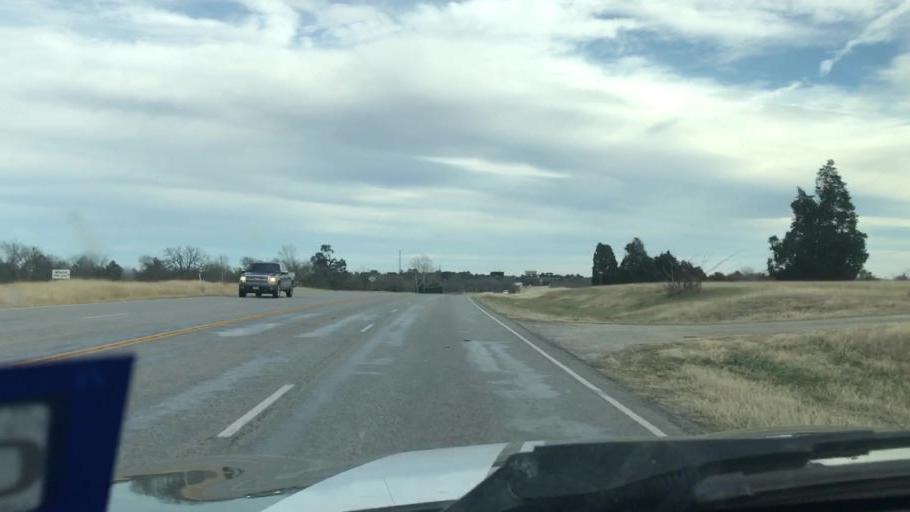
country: US
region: Texas
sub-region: Bastrop County
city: Camp Swift
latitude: 30.2965
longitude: -97.2692
